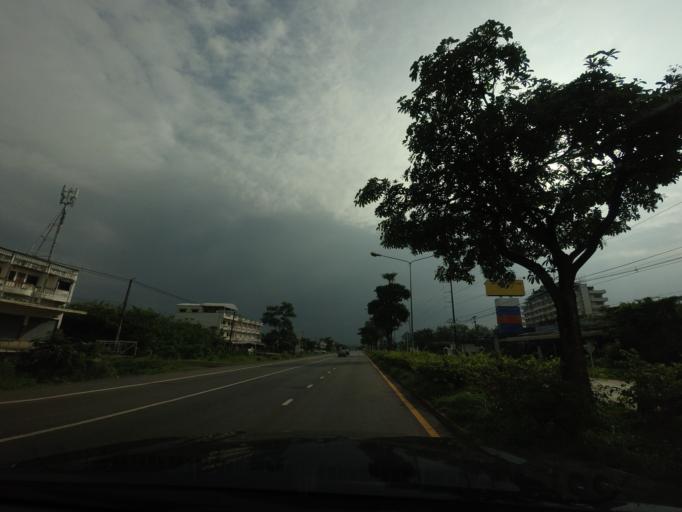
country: TH
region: Nong Khai
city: Nong Khai
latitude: 17.8798
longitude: 102.7498
